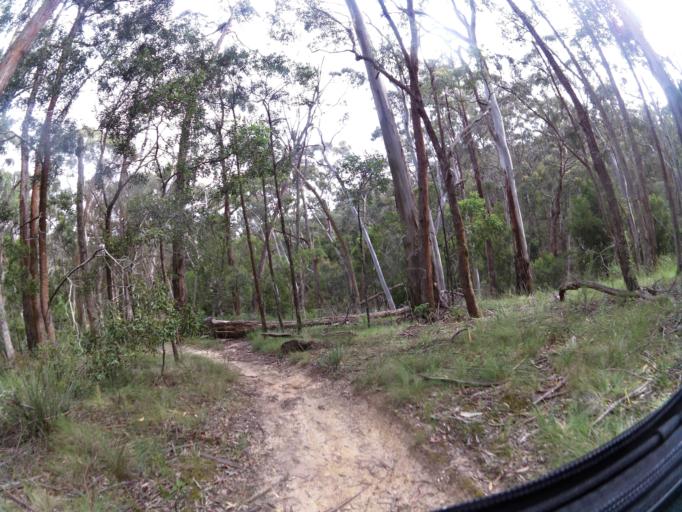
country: AU
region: Victoria
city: Brown Hill
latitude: -37.4687
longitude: 143.9089
